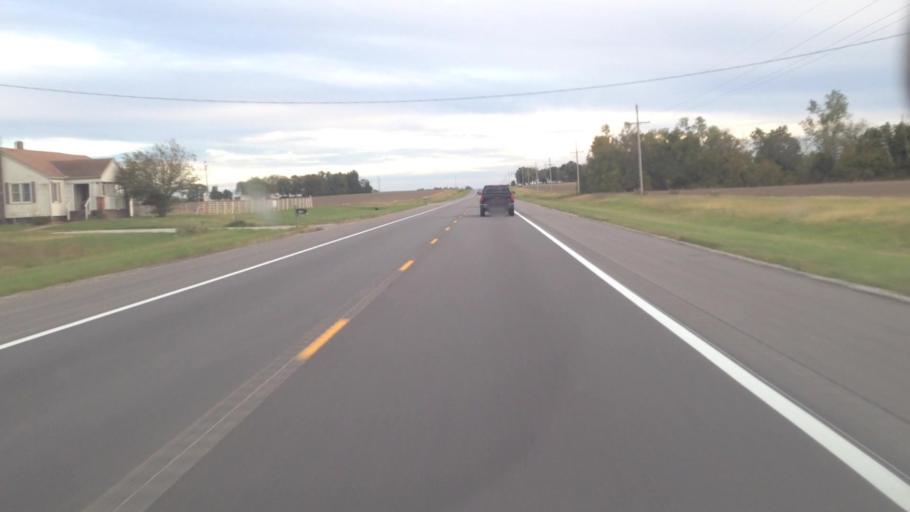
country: US
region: Kansas
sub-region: Franklin County
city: Ottawa
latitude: 38.5412
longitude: -95.2678
